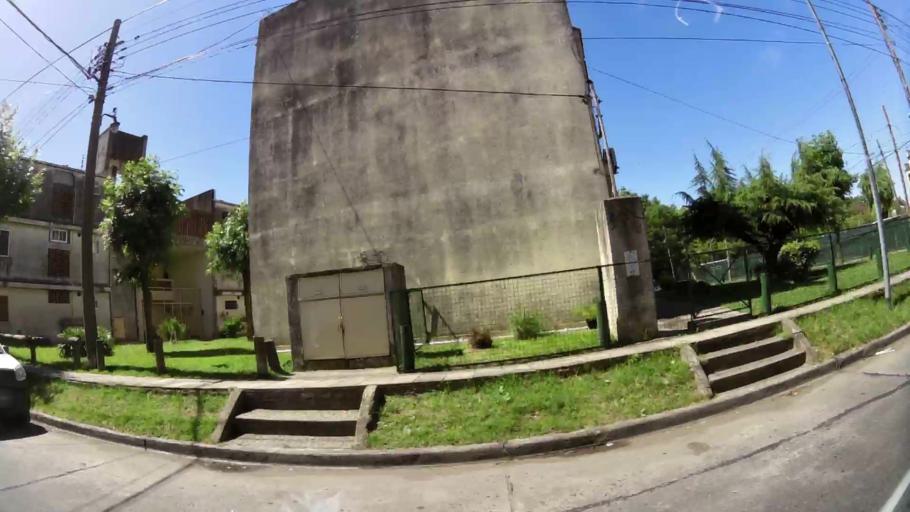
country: AR
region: Buenos Aires
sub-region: Partido de General San Martin
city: General San Martin
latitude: -34.5645
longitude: -58.5519
